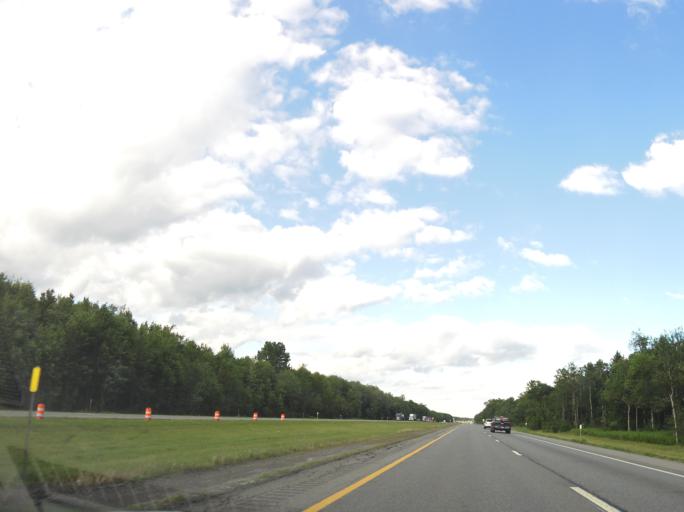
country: US
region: New York
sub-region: Erie County
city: Akron
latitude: 42.9869
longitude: -78.4591
